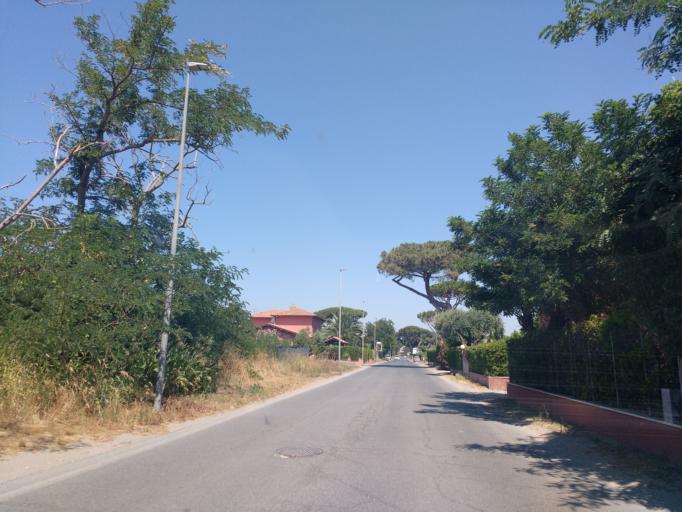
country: IT
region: Latium
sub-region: Citta metropolitana di Roma Capitale
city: Fregene
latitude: 41.8453
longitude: 12.2224
